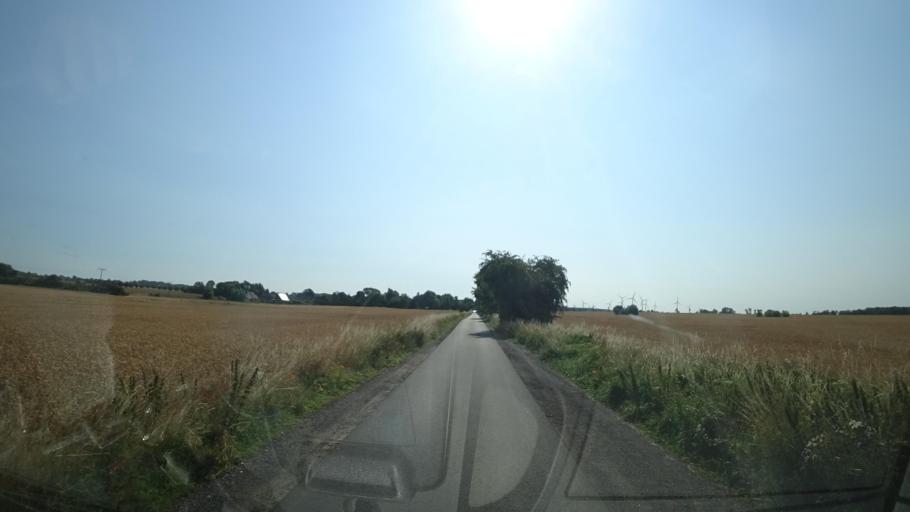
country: DE
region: Mecklenburg-Vorpommern
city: Kemnitz
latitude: 54.1201
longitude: 13.5604
